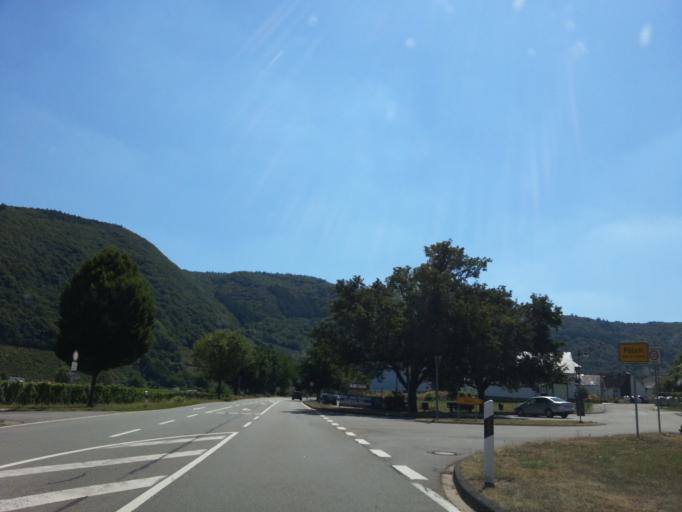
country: DE
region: Rheinland-Pfalz
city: Polich
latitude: 49.8003
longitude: 6.8489
